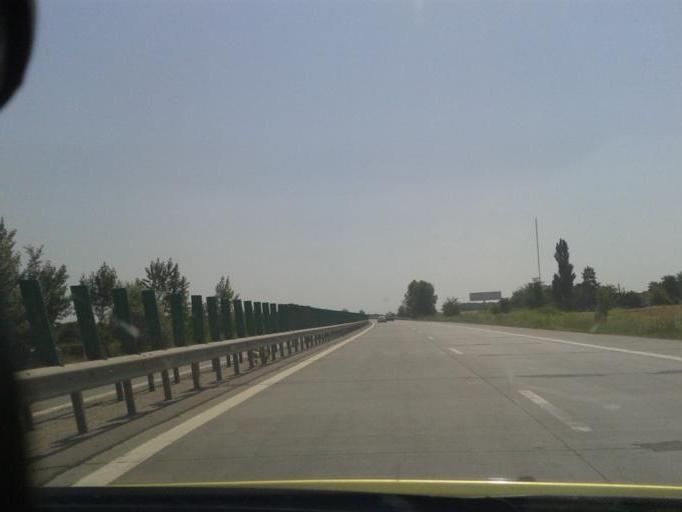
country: RO
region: Calarasi
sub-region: Comuna Fundulea
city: Fundulea
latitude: 44.4513
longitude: 26.5009
